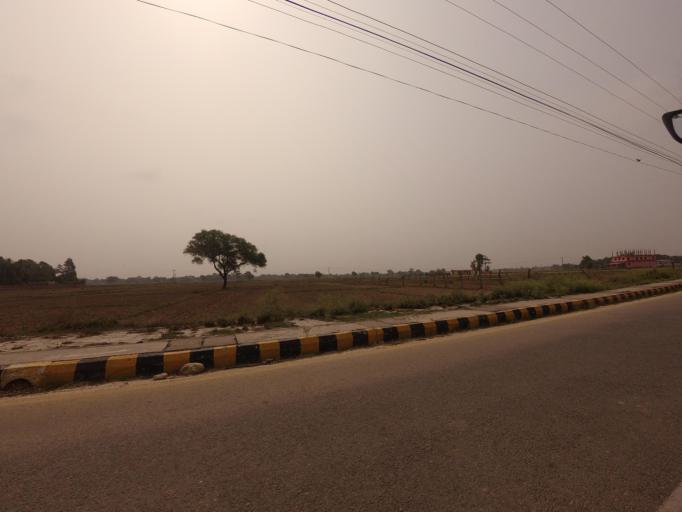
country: IN
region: Uttar Pradesh
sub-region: Maharajganj
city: Nautanwa
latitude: 27.4647
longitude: 83.2838
